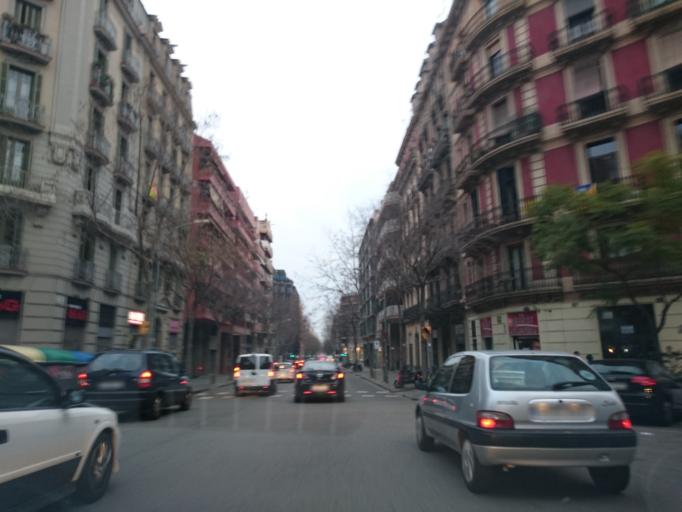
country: ES
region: Catalonia
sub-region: Provincia de Barcelona
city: Ciutat Vella
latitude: 41.3991
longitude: 2.1788
